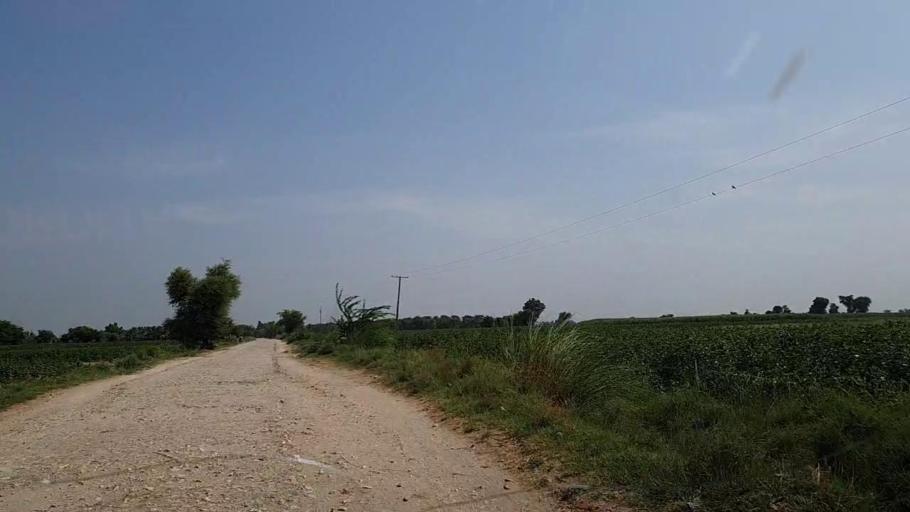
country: PK
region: Sindh
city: Khanpur
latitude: 27.7895
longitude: 69.3179
